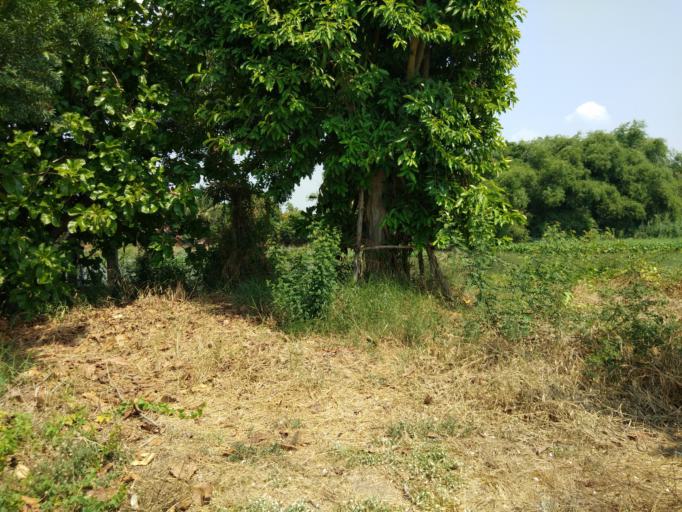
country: TH
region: Suphan Buri
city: Bang Pla Ma
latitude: 14.2853
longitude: 100.1340
